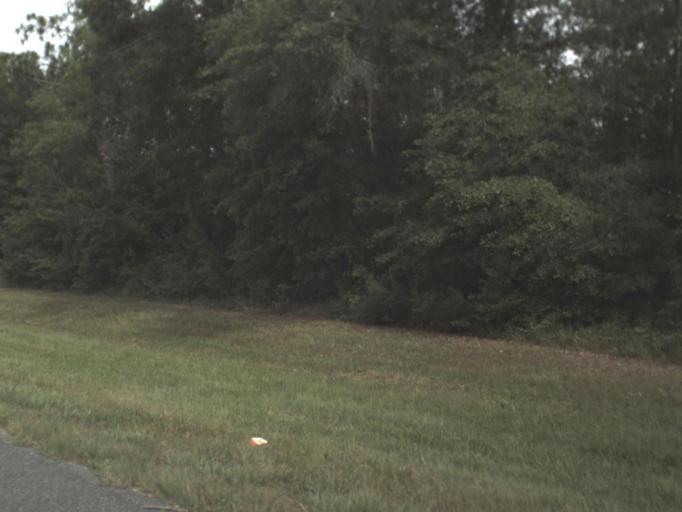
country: US
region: Florida
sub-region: Taylor County
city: Perry
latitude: 30.1002
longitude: -83.4554
